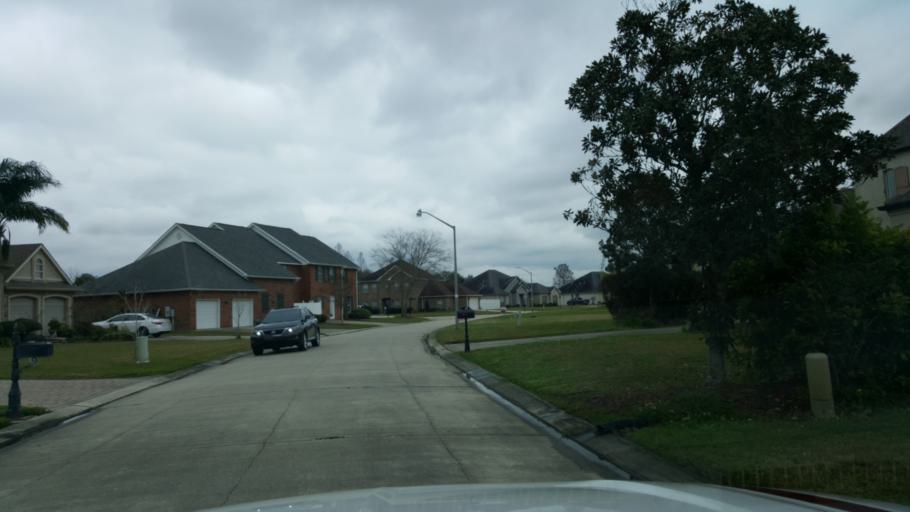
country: US
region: Louisiana
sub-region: Jefferson Parish
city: Woodmere
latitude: 29.8769
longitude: -90.0784
